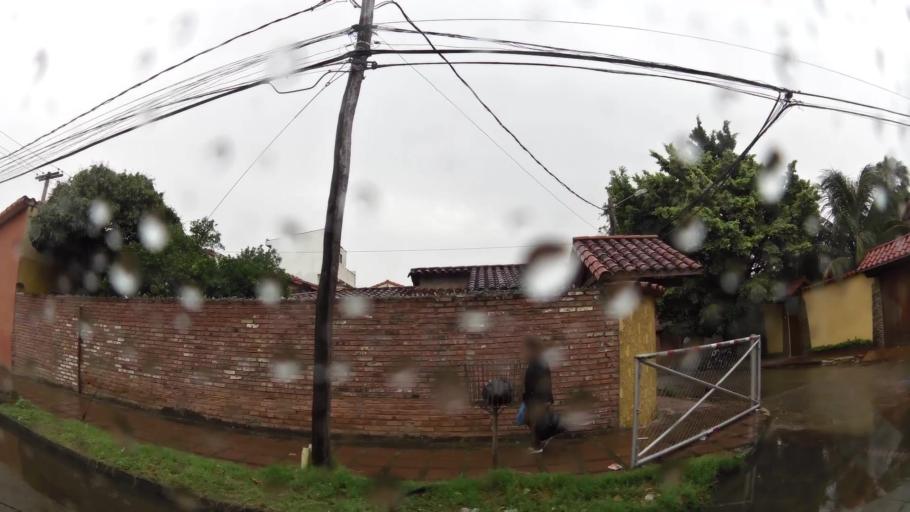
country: BO
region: Santa Cruz
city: Santa Cruz de la Sierra
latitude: -17.8096
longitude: -63.1594
